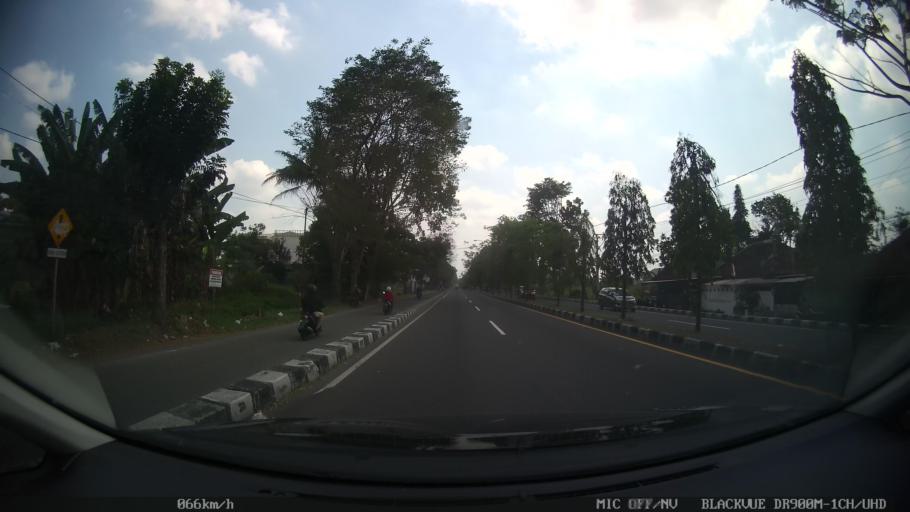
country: ID
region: Daerah Istimewa Yogyakarta
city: Gamping Lor
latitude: -7.7705
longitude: 110.3338
